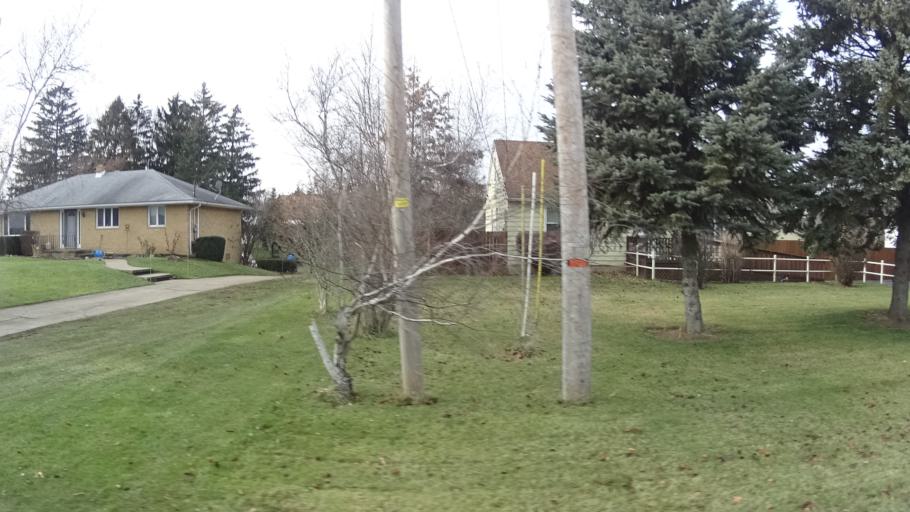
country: US
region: Ohio
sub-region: Lorain County
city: Amherst
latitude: 41.3850
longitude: -82.2437
